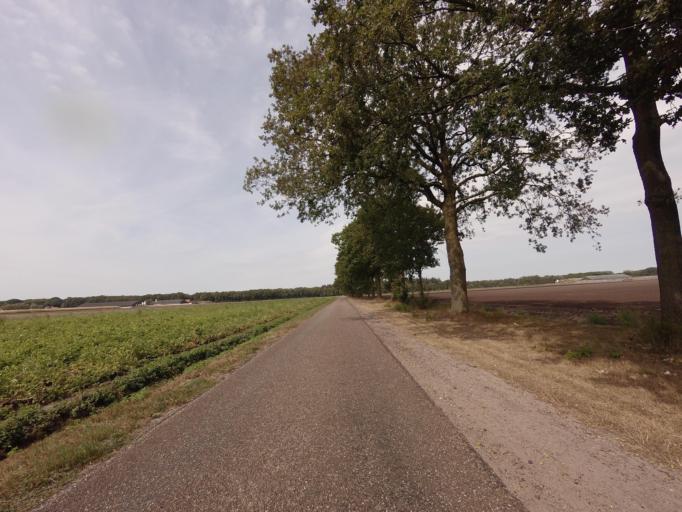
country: NL
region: North Brabant
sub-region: Gemeente Sint Anthonis
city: Sint Anthonis
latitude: 51.5555
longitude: 5.8211
